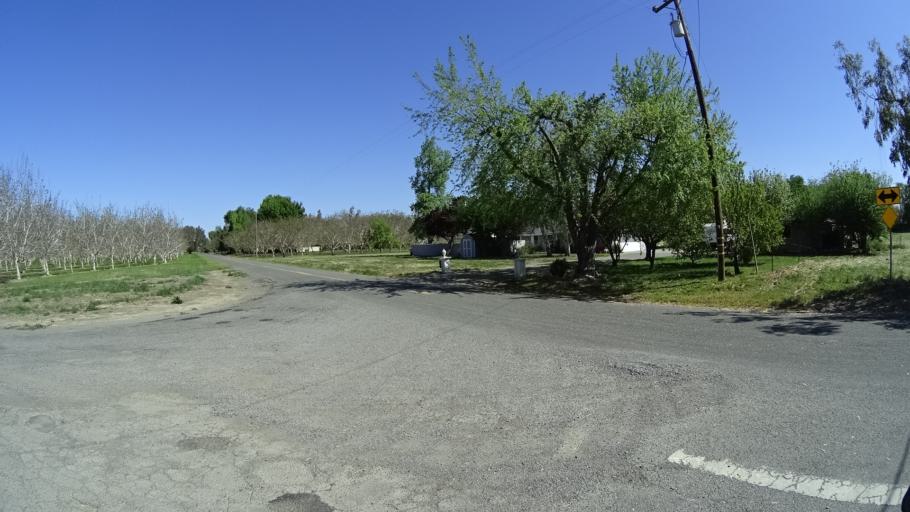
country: US
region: California
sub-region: Glenn County
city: Hamilton City
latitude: 39.7215
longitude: -122.0118
